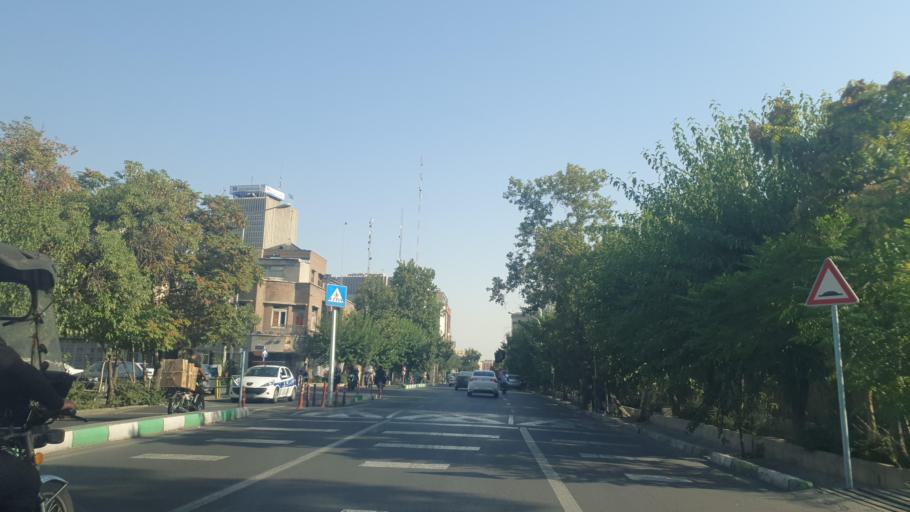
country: IR
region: Tehran
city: Tehran
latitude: 35.7100
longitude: 51.4255
